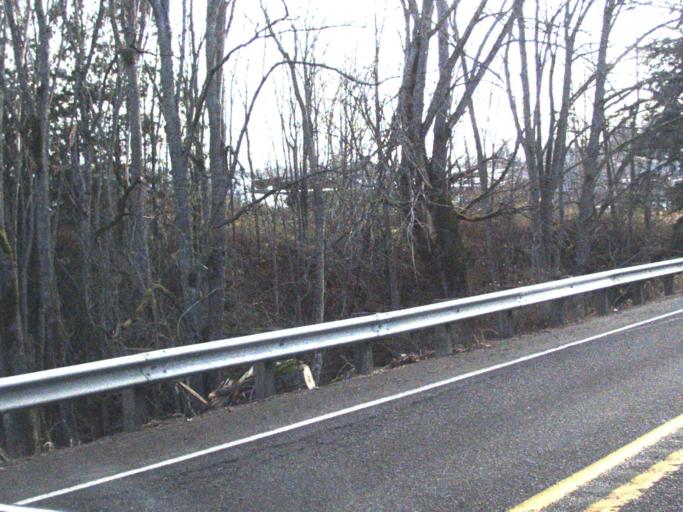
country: US
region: Washington
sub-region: Whatcom County
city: Geneva
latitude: 48.7900
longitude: -122.4212
